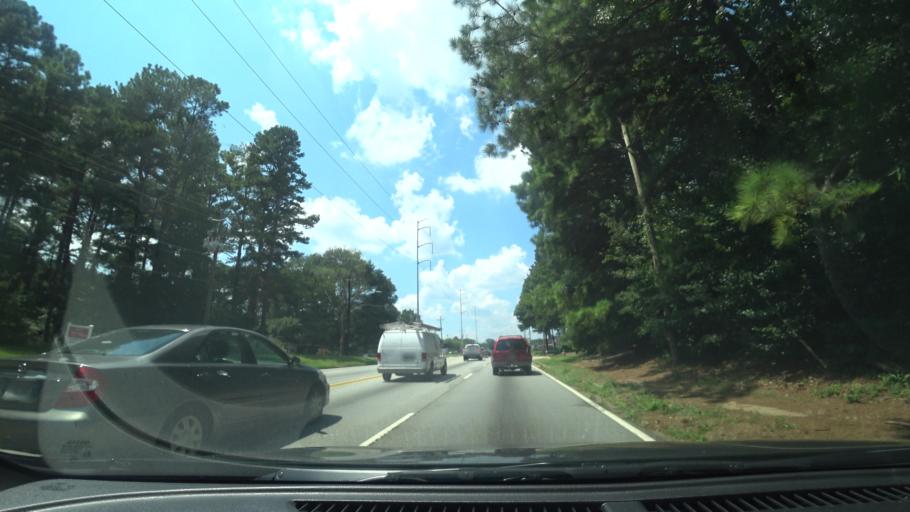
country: US
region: Georgia
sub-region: DeKalb County
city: Belvedere Park
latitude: 33.7338
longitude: -84.2102
